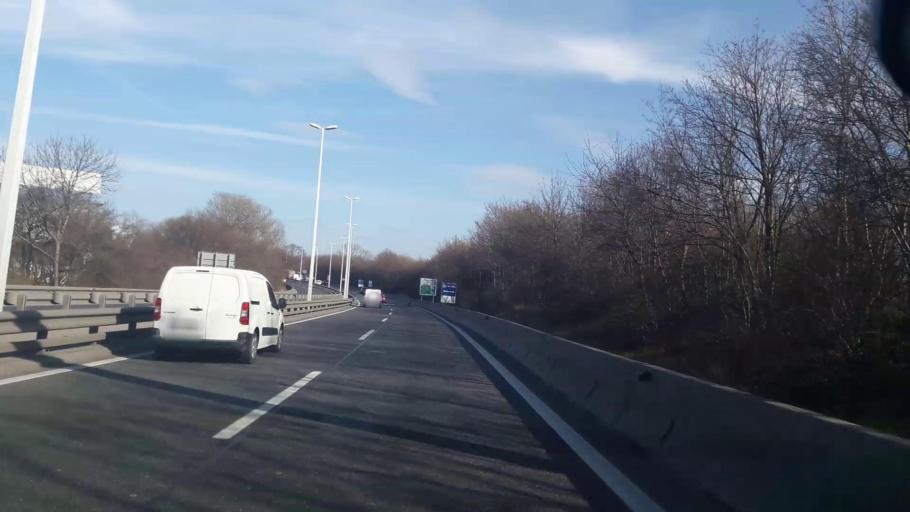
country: AT
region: Lower Austria
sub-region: Politischer Bezirk Korneuburg
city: Langenzersdorf
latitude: 48.2812
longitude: 16.3712
